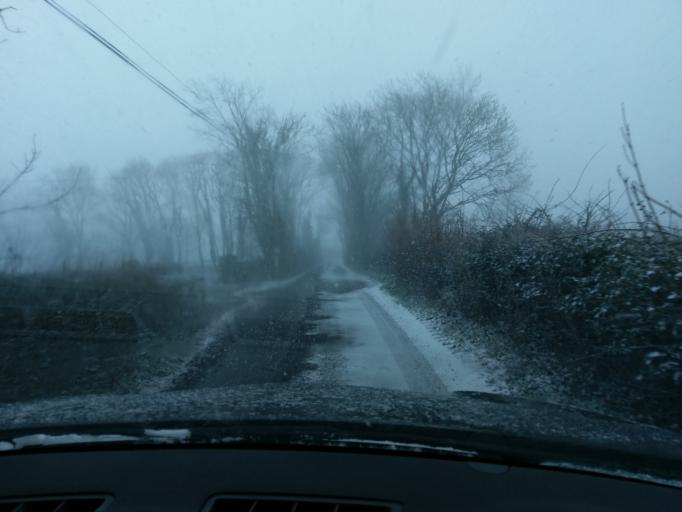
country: IE
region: Connaught
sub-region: County Galway
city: Oranmore
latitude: 53.1999
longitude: -8.9093
